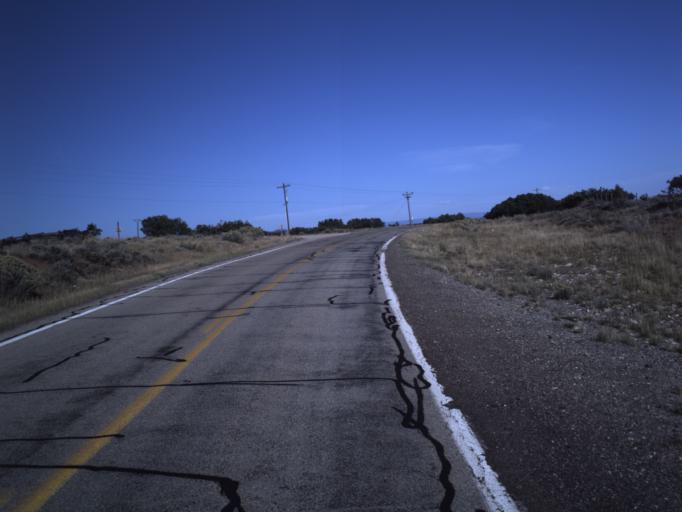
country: US
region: Utah
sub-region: Grand County
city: Moab
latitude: 38.3451
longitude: -109.1891
